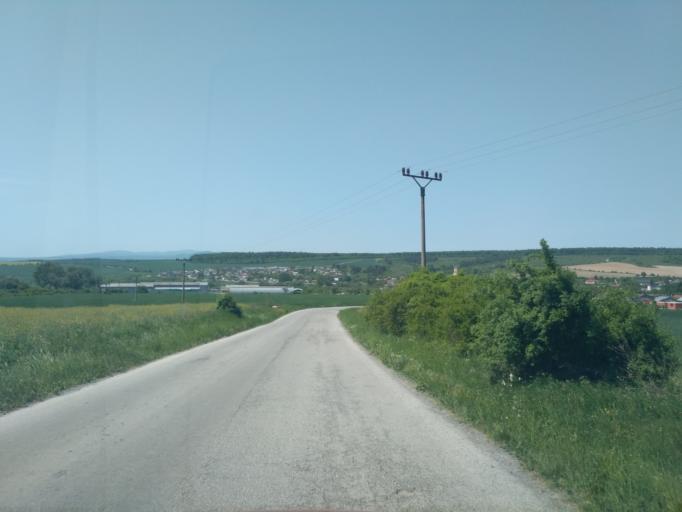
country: SK
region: Kosicky
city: Kosice
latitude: 48.8222
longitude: 21.4314
